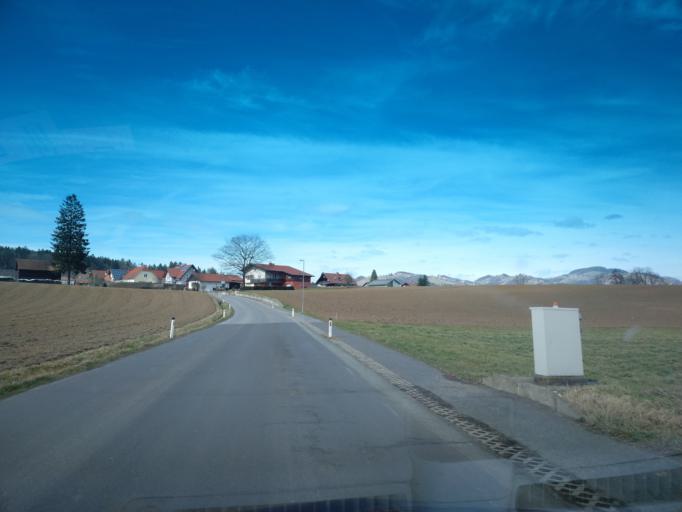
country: AT
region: Styria
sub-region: Politischer Bezirk Leibnitz
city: Grossklein
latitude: 46.7392
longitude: 15.4328
